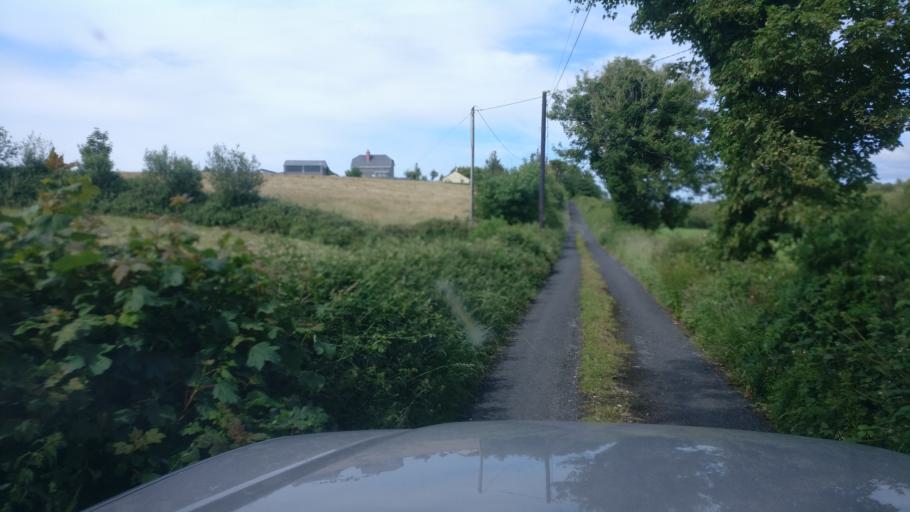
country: IE
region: Connaught
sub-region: County Galway
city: Gort
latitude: 53.0756
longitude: -8.7741
